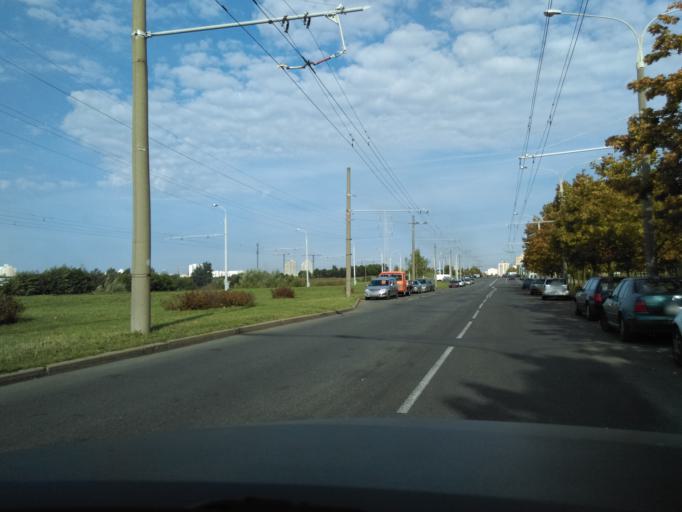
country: BY
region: Minsk
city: Minsk
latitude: 53.8562
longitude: 27.5929
